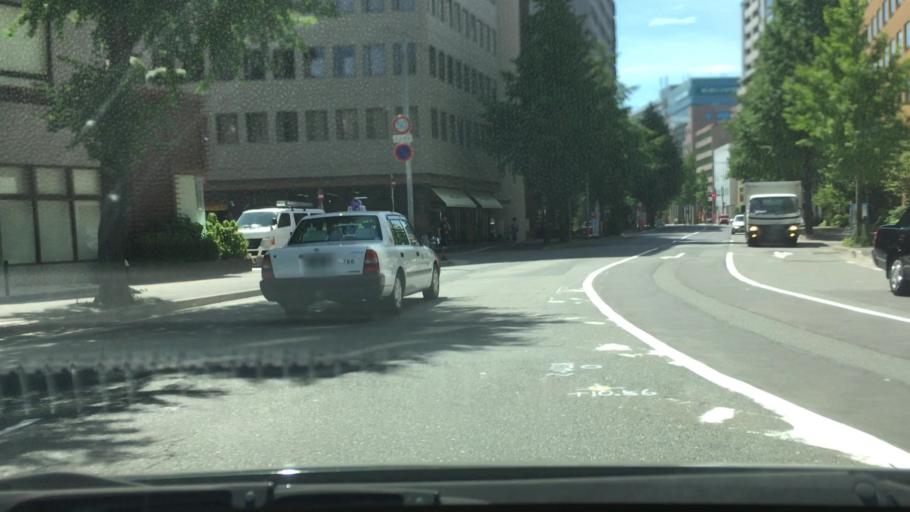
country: JP
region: Fukuoka
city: Fukuoka-shi
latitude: 33.5895
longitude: 130.4129
